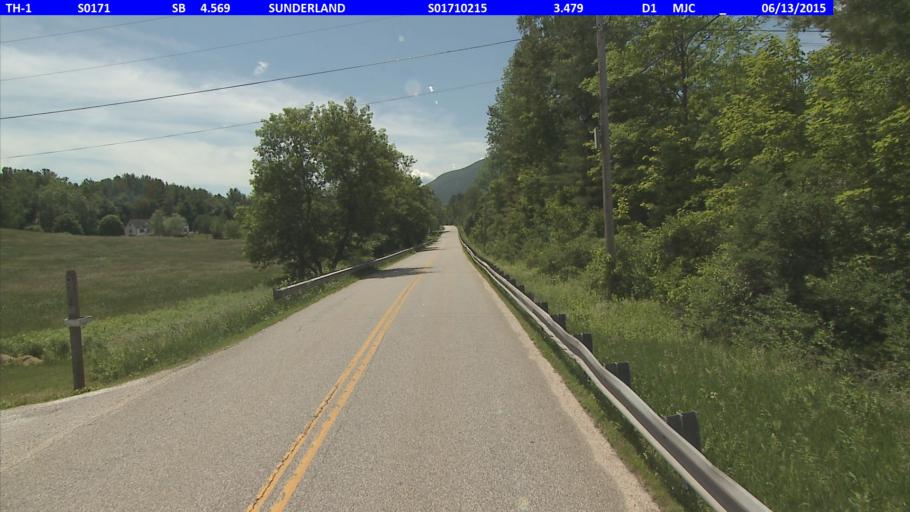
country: US
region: Vermont
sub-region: Bennington County
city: Arlington
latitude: 43.1109
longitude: -73.1118
